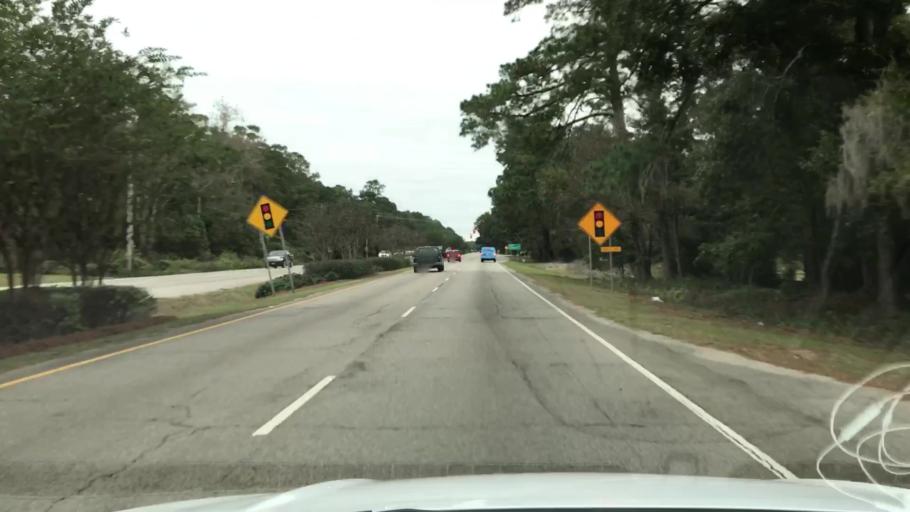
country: US
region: South Carolina
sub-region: Georgetown County
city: Murrells Inlet
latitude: 33.4891
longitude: -79.0919
